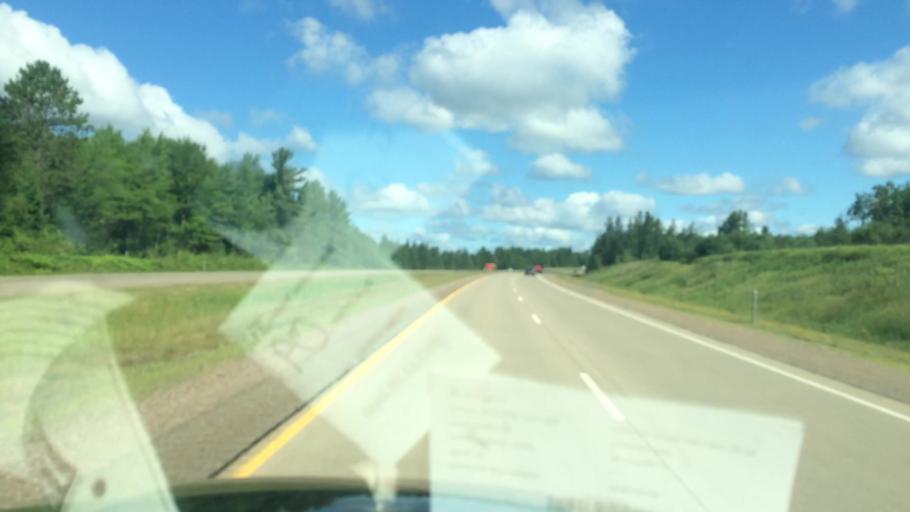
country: US
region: Wisconsin
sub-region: Lincoln County
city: Tomahawk
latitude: 45.4413
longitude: -89.6839
